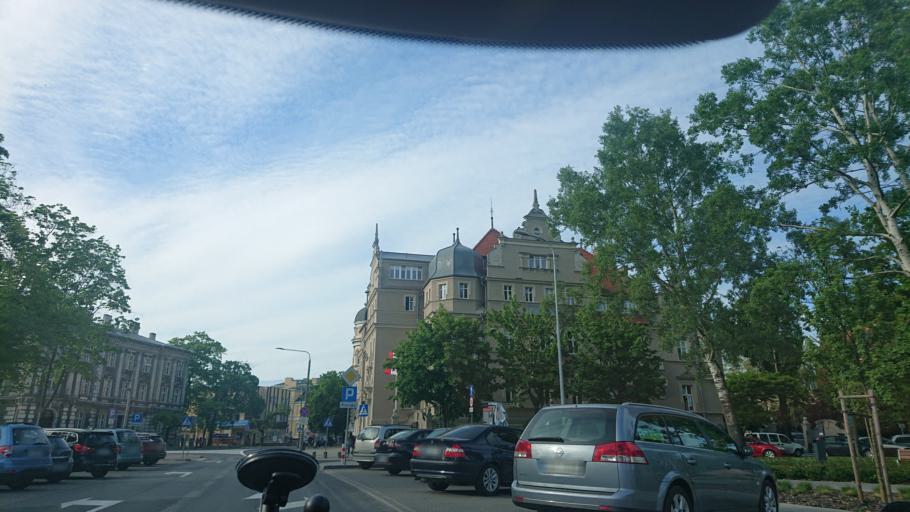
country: PL
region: Greater Poland Voivodeship
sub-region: Powiat gnieznienski
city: Gniezno
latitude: 52.5304
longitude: 17.6024
